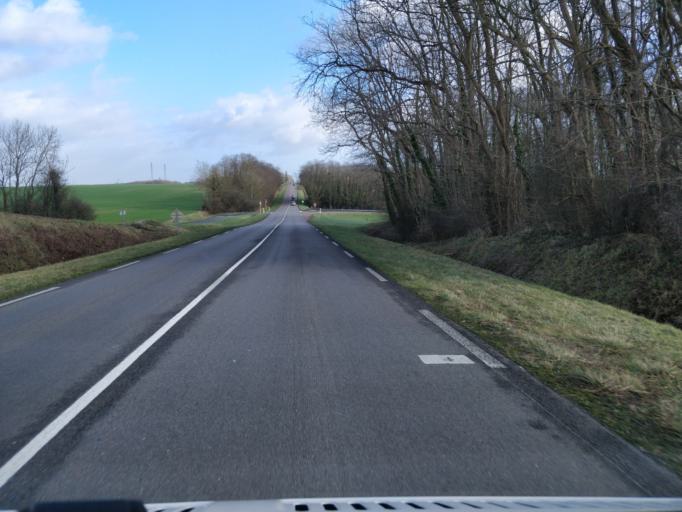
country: FR
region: Bourgogne
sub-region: Departement de l'Yonne
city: Paron
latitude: 48.1824
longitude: 3.2228
